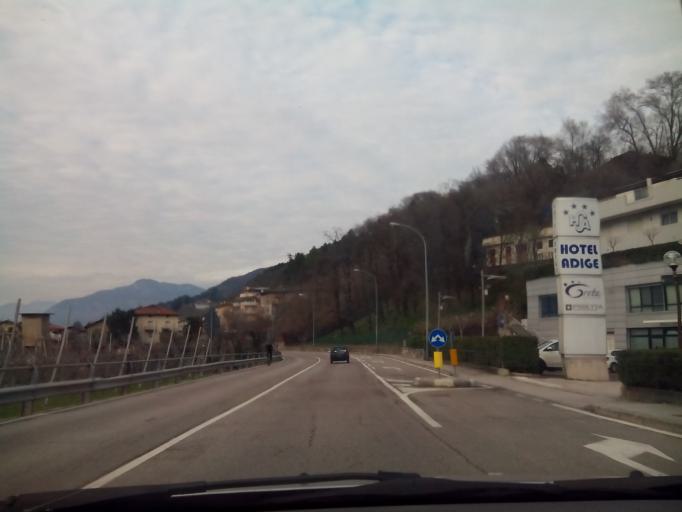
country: IT
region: Trentino-Alto Adige
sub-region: Provincia di Trento
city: Mattarello
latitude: 46.0139
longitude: 11.1316
